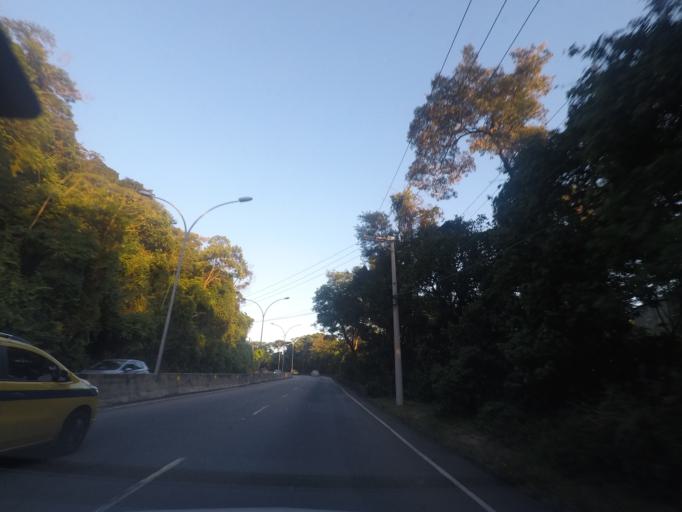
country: BR
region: Rio de Janeiro
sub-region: Rio De Janeiro
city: Rio de Janeiro
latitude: -22.9231
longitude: -43.3071
